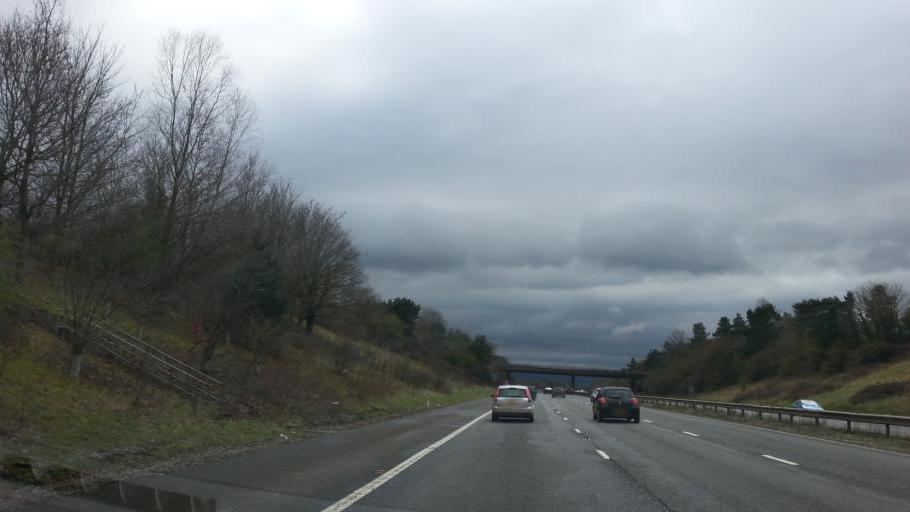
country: GB
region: England
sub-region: Somerset
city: Creech Saint Michael
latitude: 51.0499
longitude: -3.0275
